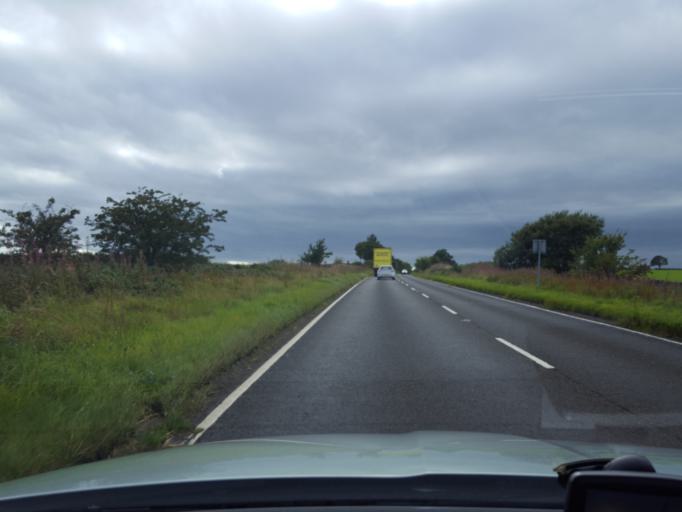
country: GB
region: Scotland
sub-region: Perth and Kinross
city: Milnathort
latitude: 56.2509
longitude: -3.3625
